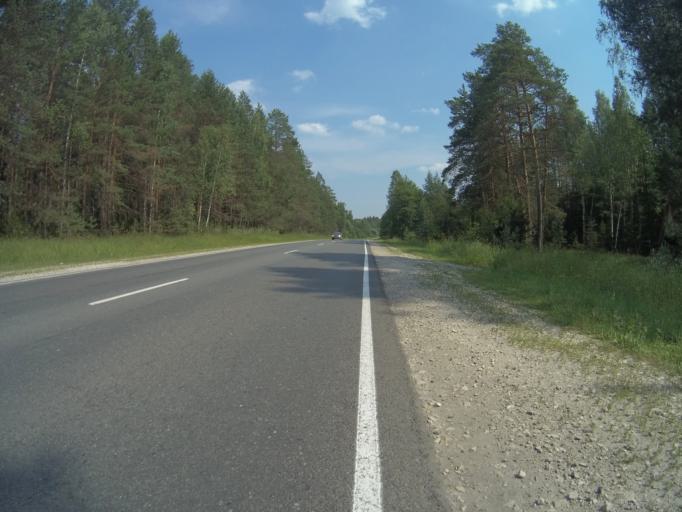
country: RU
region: Vladimir
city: Muromtsevo
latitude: 55.9556
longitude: 40.9963
